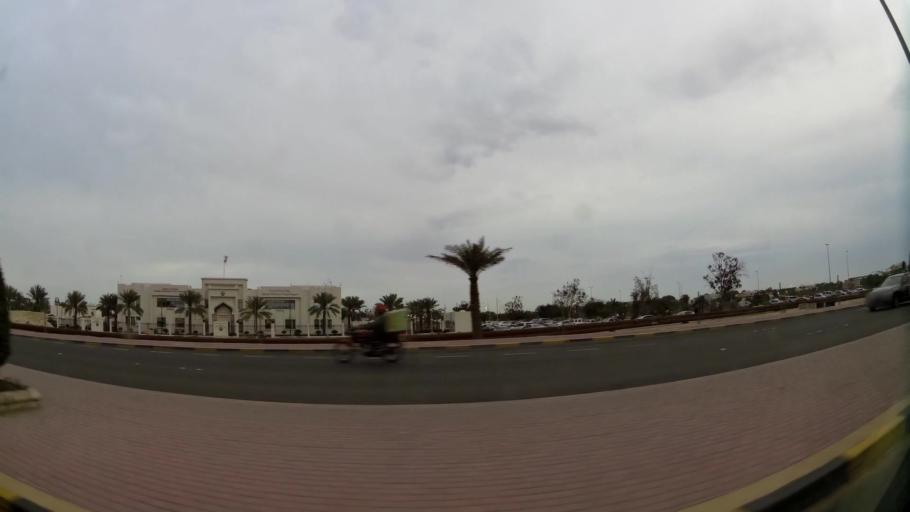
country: BH
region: Northern
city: Ar Rifa'
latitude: 26.1340
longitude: 50.5370
